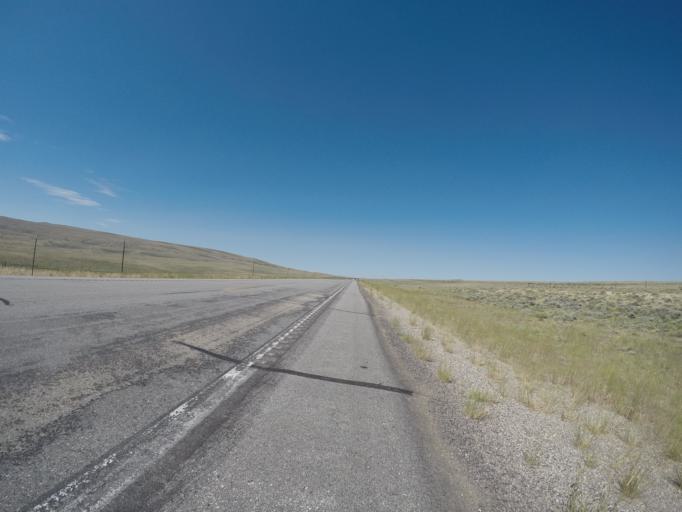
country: US
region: Wyoming
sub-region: Carbon County
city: Saratoga
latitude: 41.7986
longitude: -106.7154
